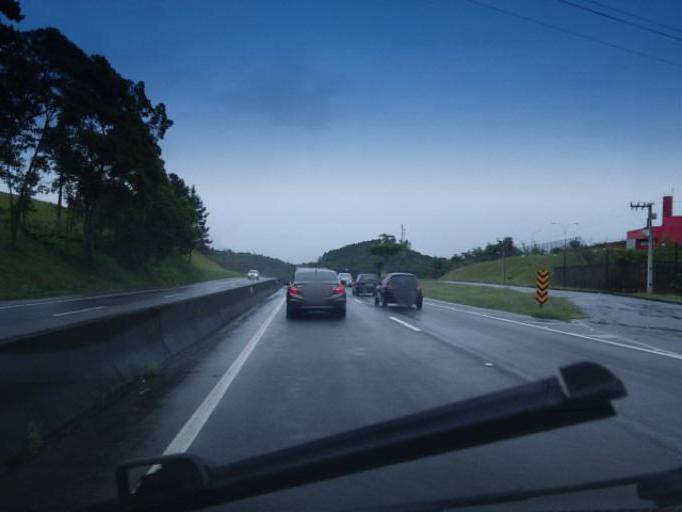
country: BR
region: Santa Catarina
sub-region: Joinville
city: Joinville
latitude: -26.4480
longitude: -48.7905
